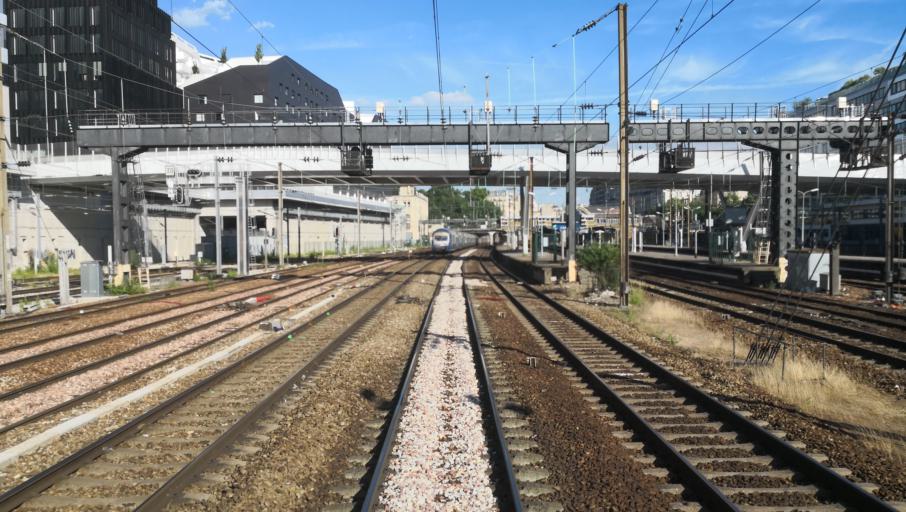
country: FR
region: Ile-de-France
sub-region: Paris
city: Saint-Ouen
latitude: 48.8845
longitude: 2.3269
